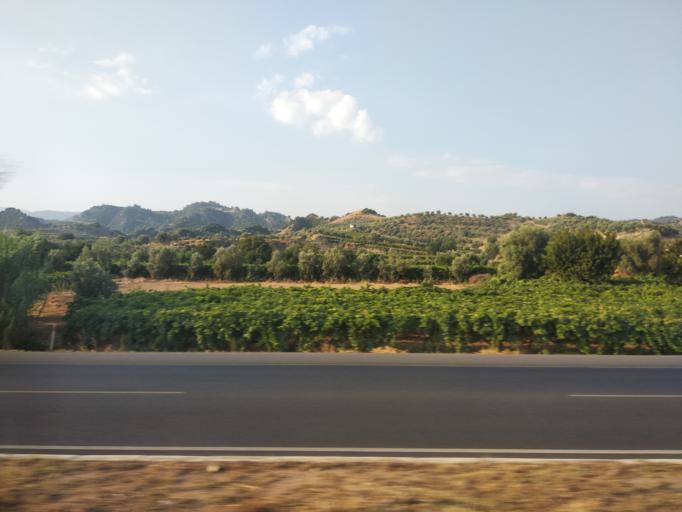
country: TR
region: Manisa
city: Ahmetli
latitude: 38.5079
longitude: 27.9881
